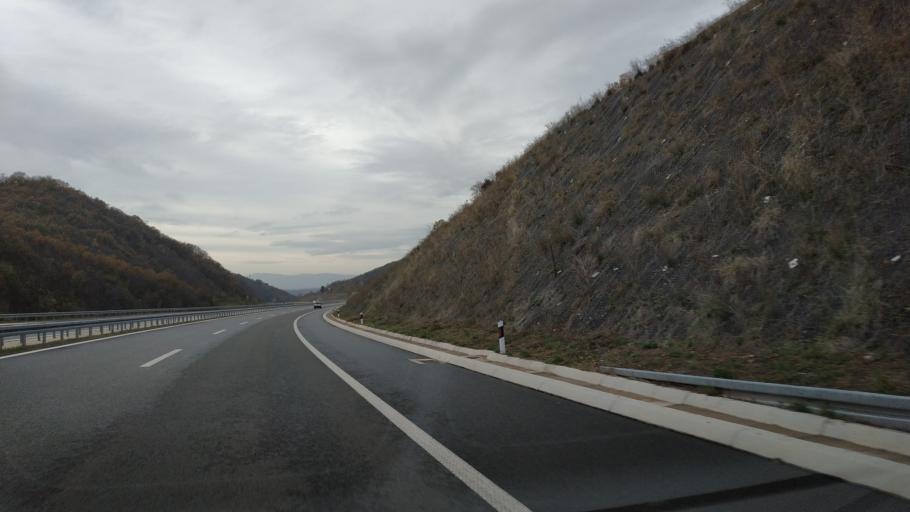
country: RS
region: Central Serbia
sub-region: Nisavski Okrug
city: Niska Banja
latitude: 43.2962
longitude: 22.0821
